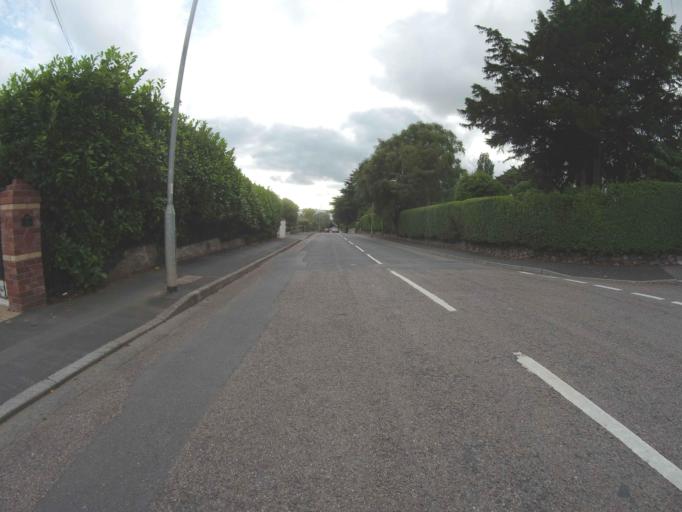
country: GB
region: England
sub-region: Devon
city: Exmouth
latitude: 50.6187
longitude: -3.3899
